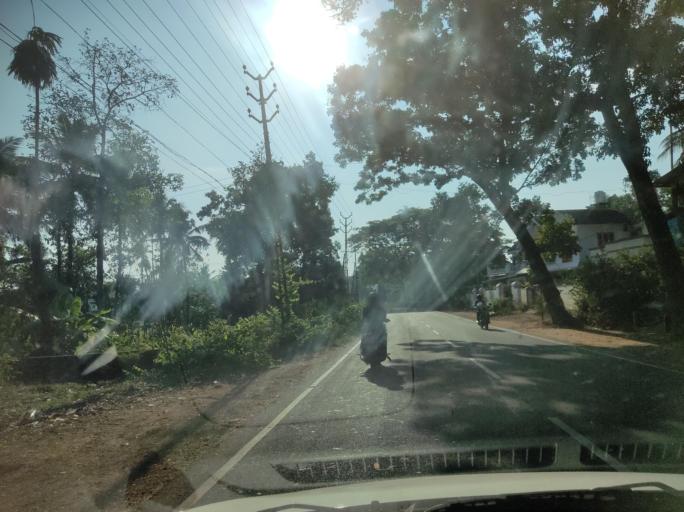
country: IN
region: Kerala
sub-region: Alappuzha
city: Kattanam
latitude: 9.1739
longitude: 76.5827
